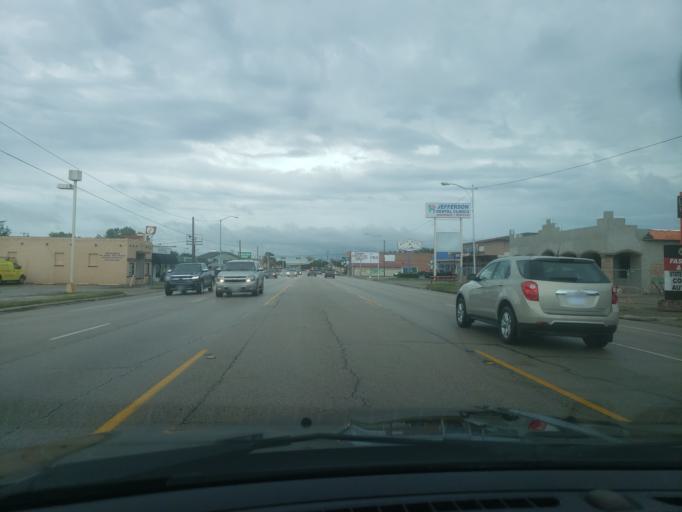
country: US
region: Texas
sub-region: Dallas County
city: Grand Prairie
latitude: 32.7457
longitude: -97.0000
